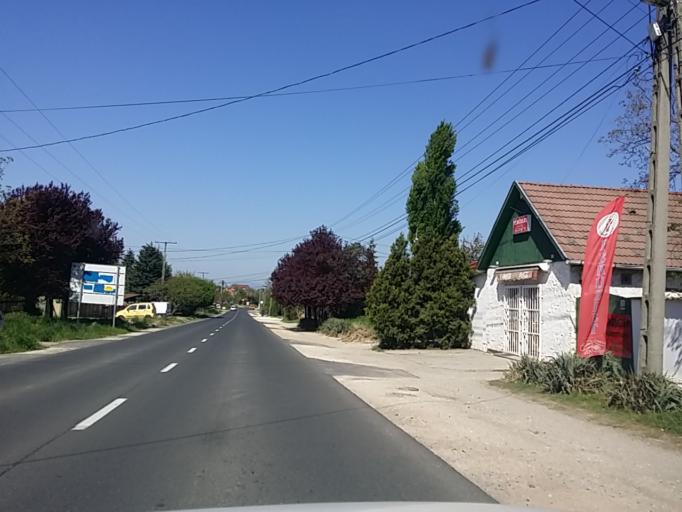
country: HU
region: Pest
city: Mogyorod
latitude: 47.5970
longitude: 19.2661
